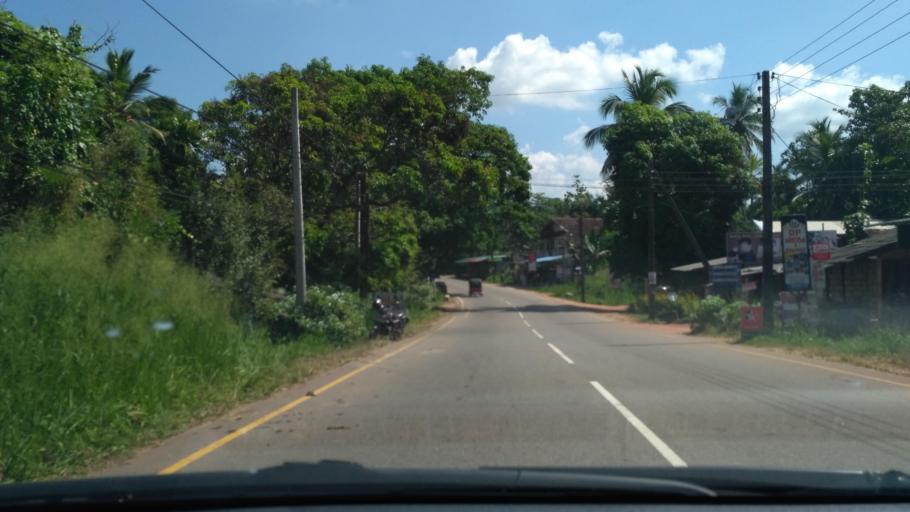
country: LK
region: North Western
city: Kuliyapitiya
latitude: 7.3249
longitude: 80.0415
